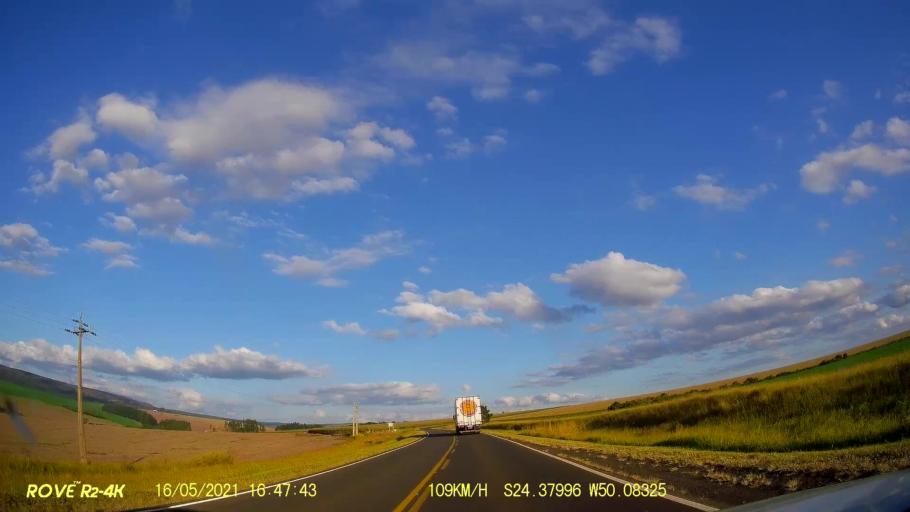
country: BR
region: Parana
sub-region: Pirai Do Sul
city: Pirai do Sul
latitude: -24.3800
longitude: -50.0832
